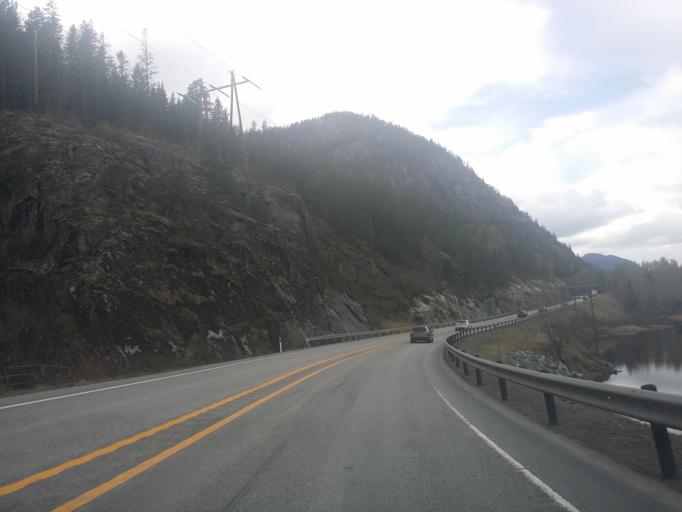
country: NO
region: Buskerud
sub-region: Nes
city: Nesbyen
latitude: 60.4576
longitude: 9.2639
